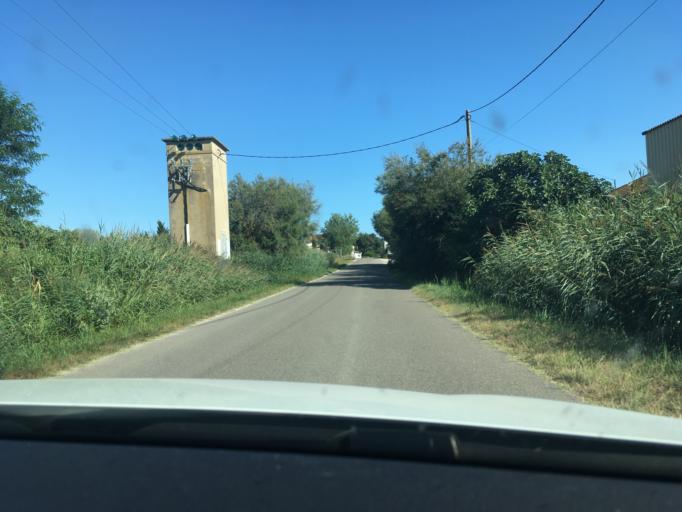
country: FR
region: Provence-Alpes-Cote d'Azur
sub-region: Departement des Bouches-du-Rhone
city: Saintes-Maries-de-la-Mer
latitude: 43.5456
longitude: 4.3459
